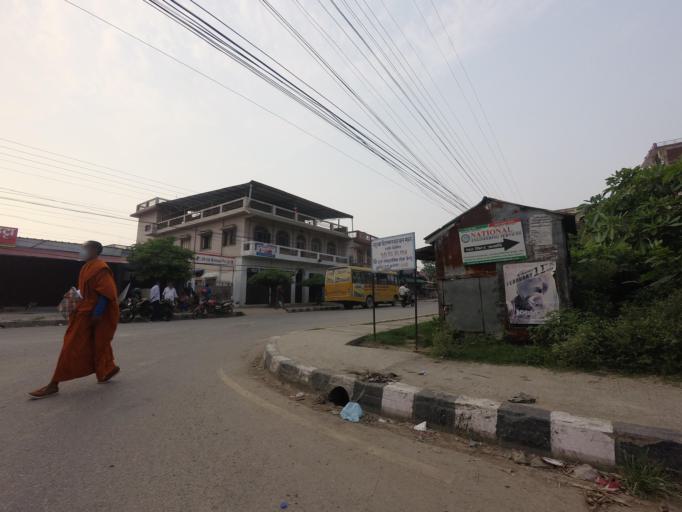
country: NP
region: Western Region
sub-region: Lumbini Zone
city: Bhairahawa
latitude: 27.4979
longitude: 83.4476
